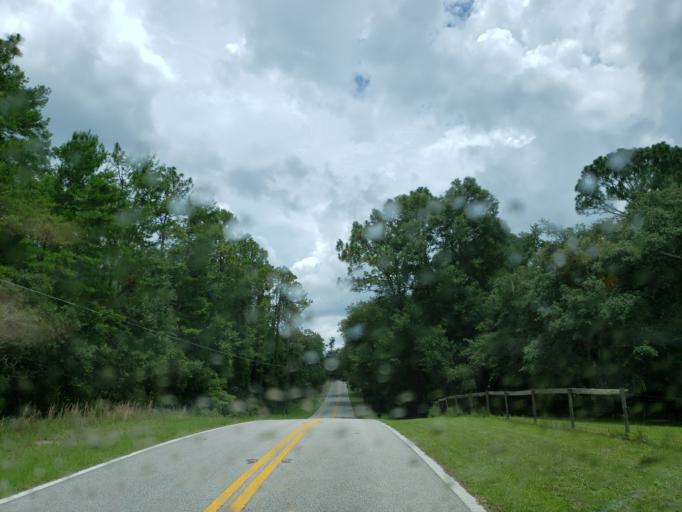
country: US
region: Florida
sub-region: Citrus County
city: Floral City
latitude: 28.6616
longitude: -82.3166
